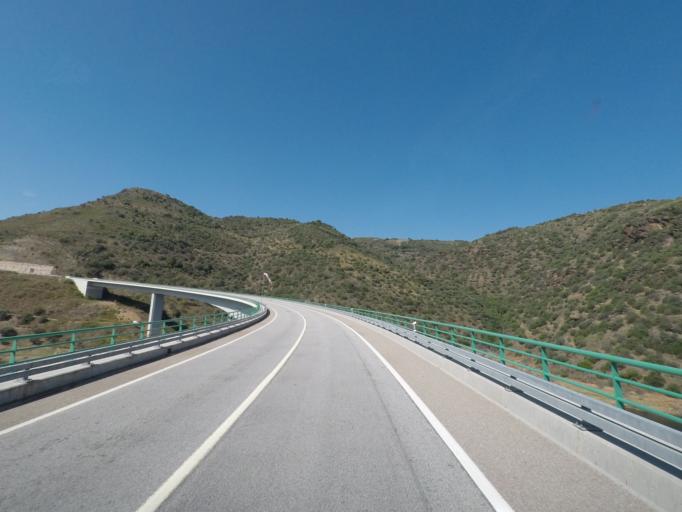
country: PT
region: Braganca
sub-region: Alfandega da Fe
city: Alfandega da Fe
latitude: 41.2872
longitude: -6.8736
